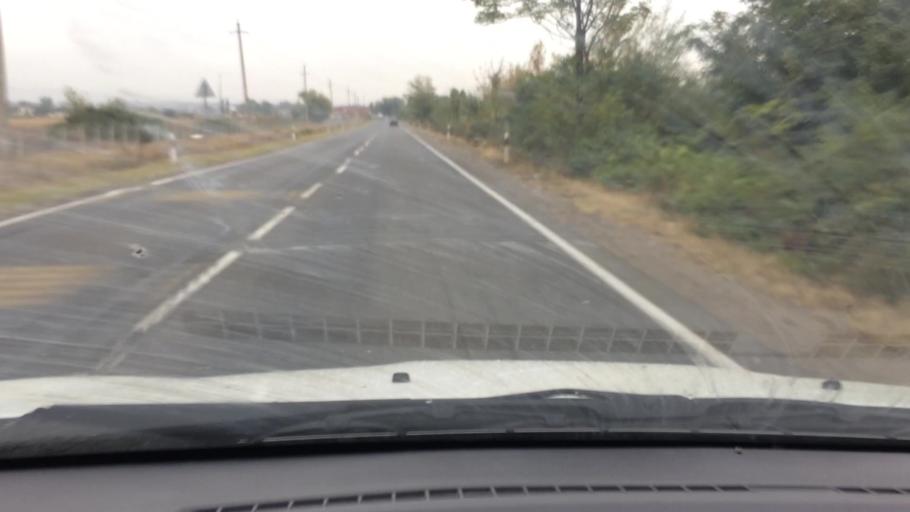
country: GE
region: Kvemo Kartli
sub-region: Marneuli
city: Marneuli
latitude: 41.4667
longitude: 44.8043
